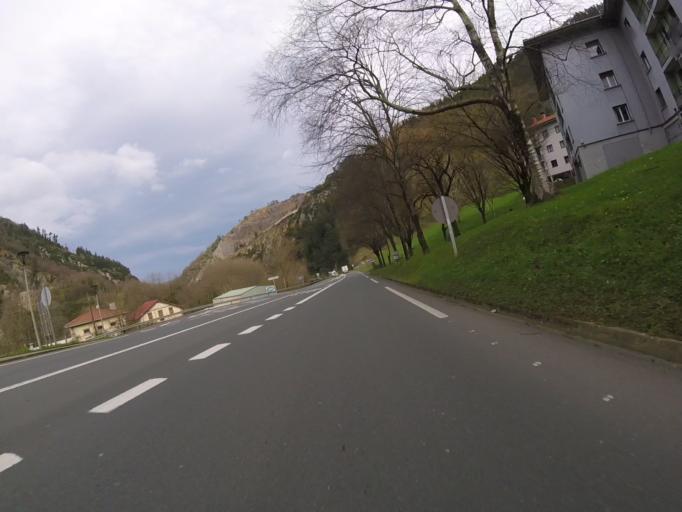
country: ES
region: Basque Country
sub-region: Provincia de Guipuzcoa
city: Cestona
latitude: 43.2420
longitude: -2.2591
